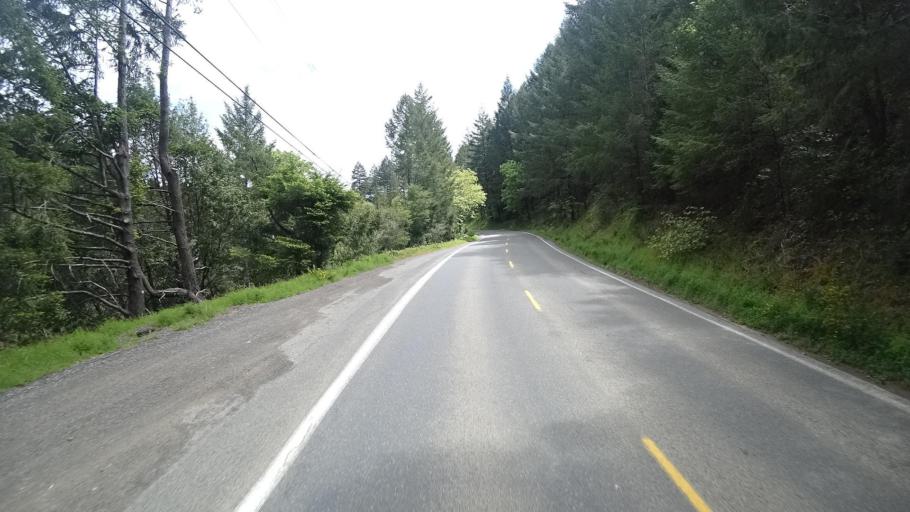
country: US
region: California
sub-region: Humboldt County
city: Redway
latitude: 40.1292
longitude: -123.8656
